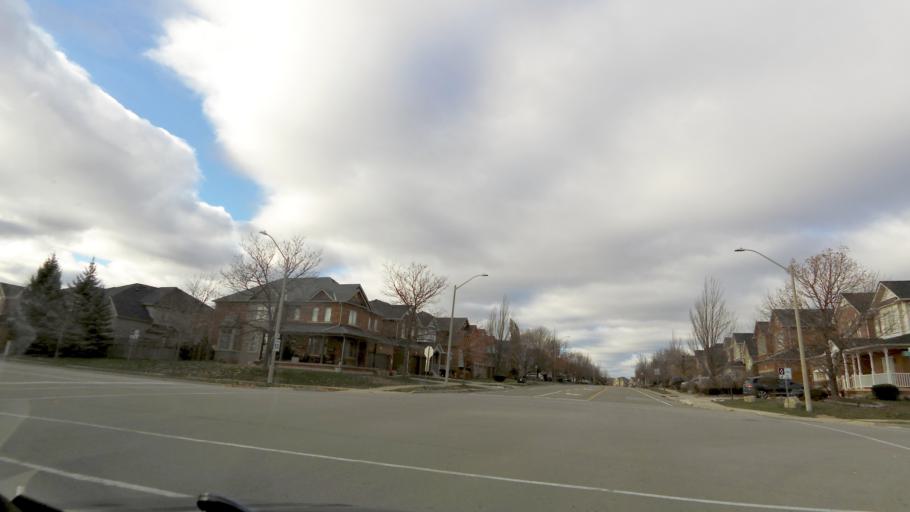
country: CA
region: Ontario
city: Oakville
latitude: 43.4913
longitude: -79.6930
